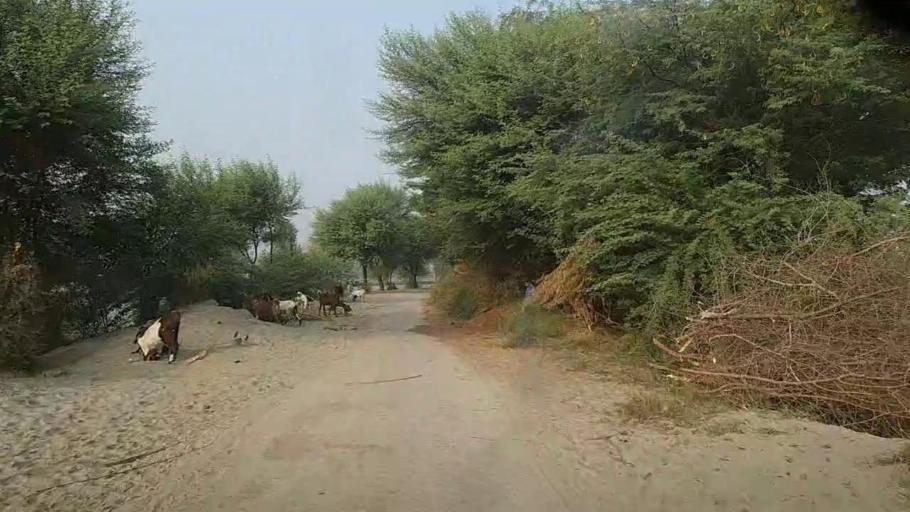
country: PK
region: Sindh
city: Bozdar
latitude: 27.1619
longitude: 68.6608
